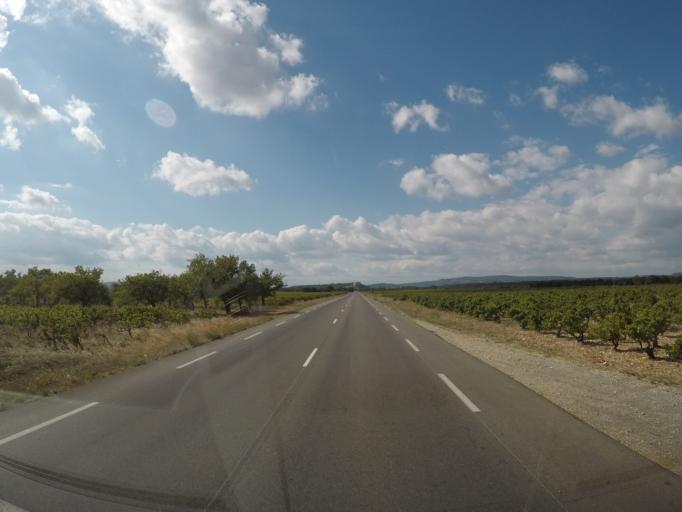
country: FR
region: Rhone-Alpes
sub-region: Departement de la Drome
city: Suze-la-Rousse
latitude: 44.2865
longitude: 4.8651
